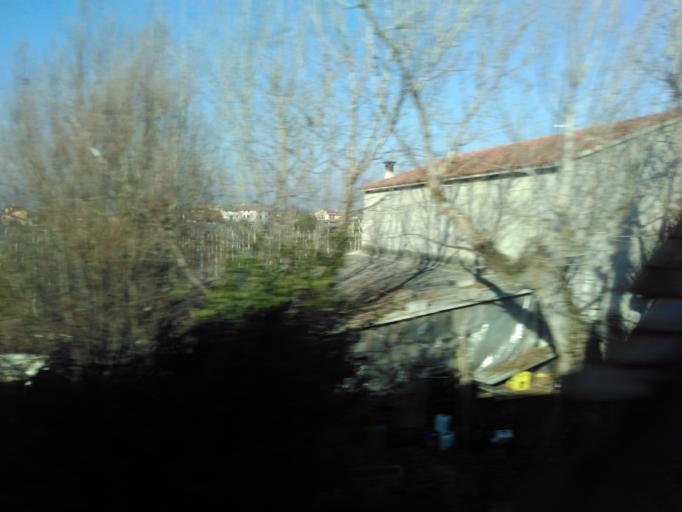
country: IT
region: Veneto
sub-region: Provincia di Verona
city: Locara
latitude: 45.4089
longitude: 11.3268
